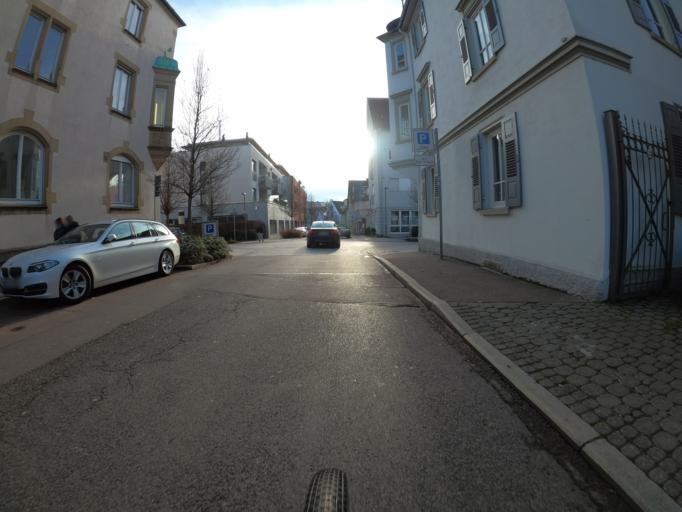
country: DE
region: Baden-Wuerttemberg
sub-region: Regierungsbezirk Stuttgart
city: Goeppingen
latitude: 48.7053
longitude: 9.6502
